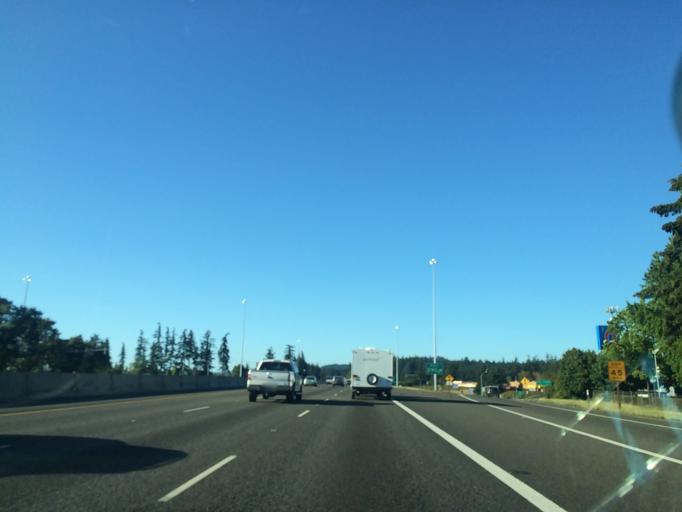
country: US
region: Oregon
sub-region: Washington County
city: Durham
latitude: 45.3939
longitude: -122.7481
